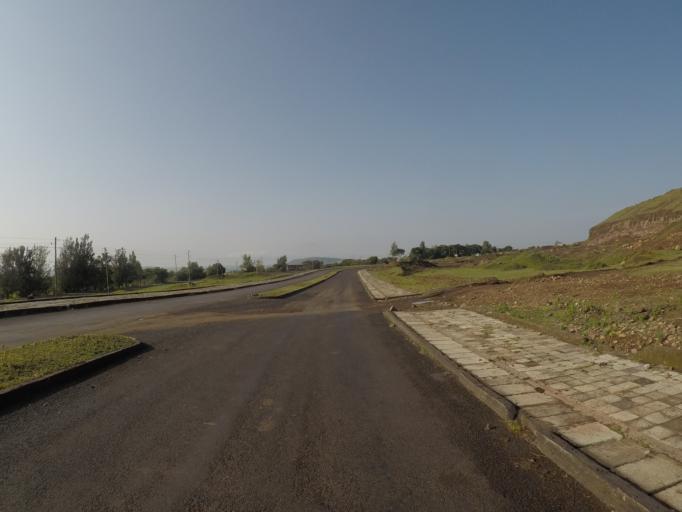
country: ET
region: Amhara
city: Gondar
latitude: 12.5248
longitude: 37.4307
